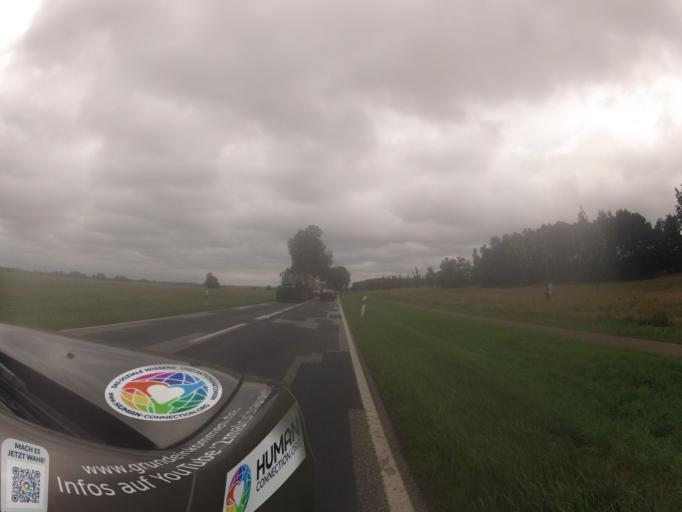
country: DE
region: Mecklenburg-Vorpommern
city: Jatznick
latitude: 53.5605
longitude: 13.9656
